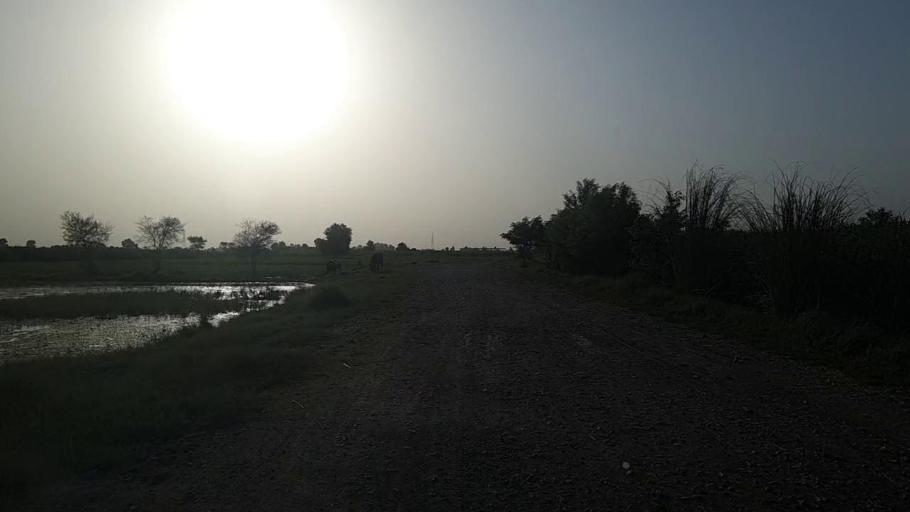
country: PK
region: Sindh
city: Naushahro Firoz
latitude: 26.8059
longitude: 68.1126
